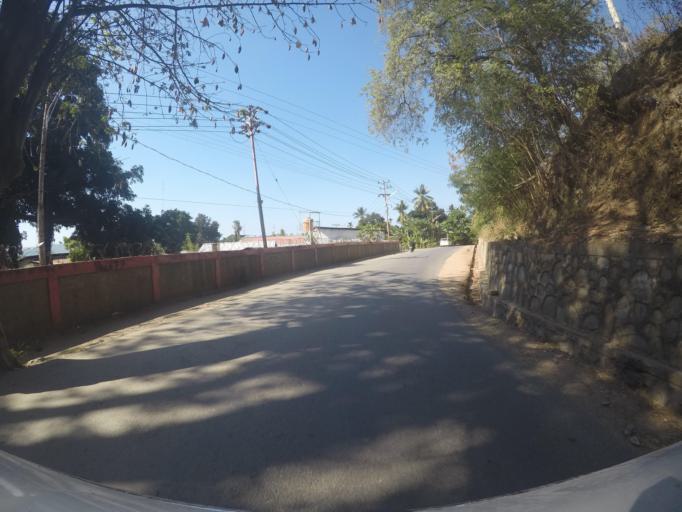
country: TL
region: Dili
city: Dili
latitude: -8.5667
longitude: 125.5484
